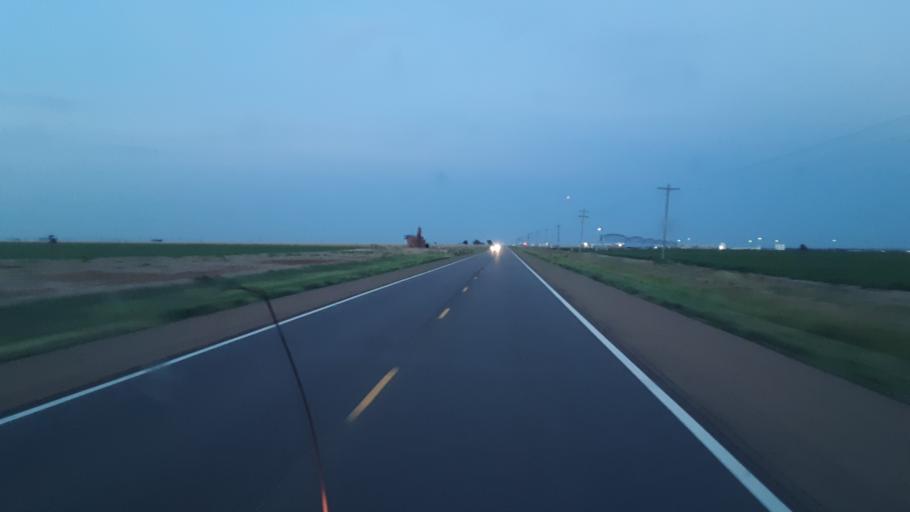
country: US
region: Kansas
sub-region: Finney County
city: Holcomb
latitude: 38.0034
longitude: -101.0460
